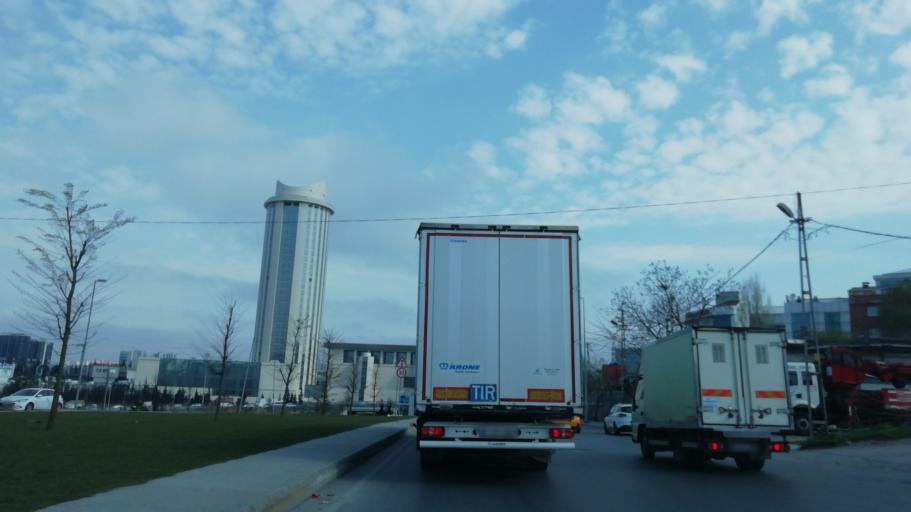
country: TR
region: Istanbul
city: Mahmutbey
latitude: 41.0608
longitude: 28.8251
